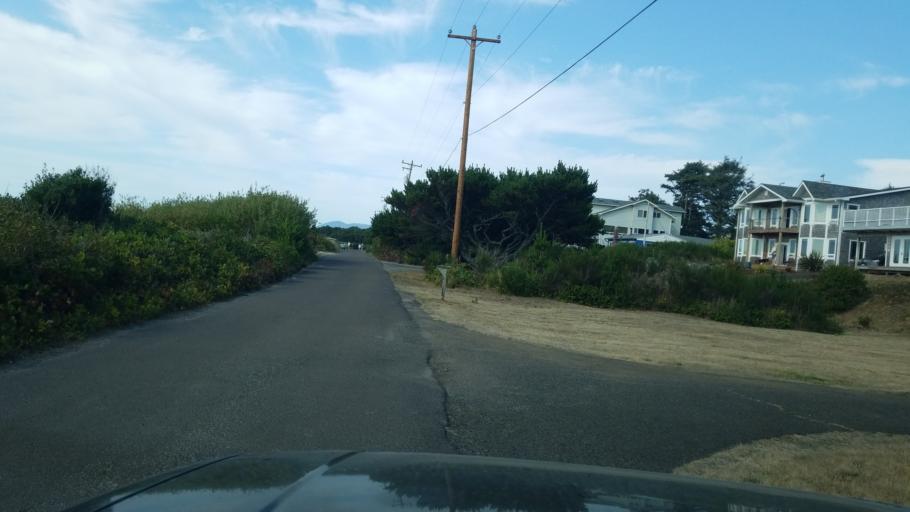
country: US
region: Oregon
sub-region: Tillamook County
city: Rockaway Beach
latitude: 45.5928
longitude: -123.9487
